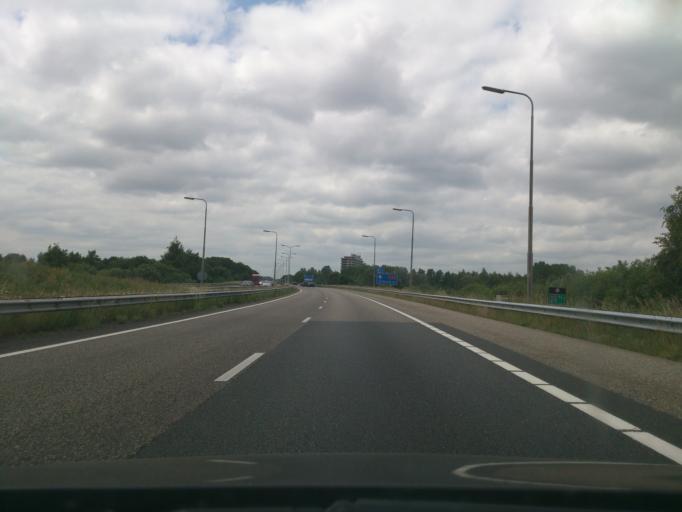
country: NL
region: North Brabant
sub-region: Gemeente Vught
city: Vught
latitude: 51.6685
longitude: 5.3074
